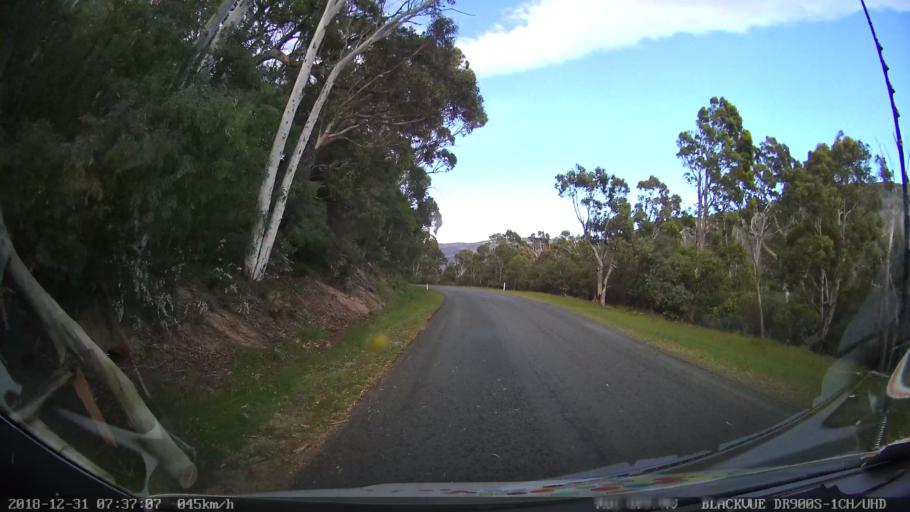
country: AU
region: New South Wales
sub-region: Snowy River
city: Jindabyne
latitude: -36.3438
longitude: 148.4388
